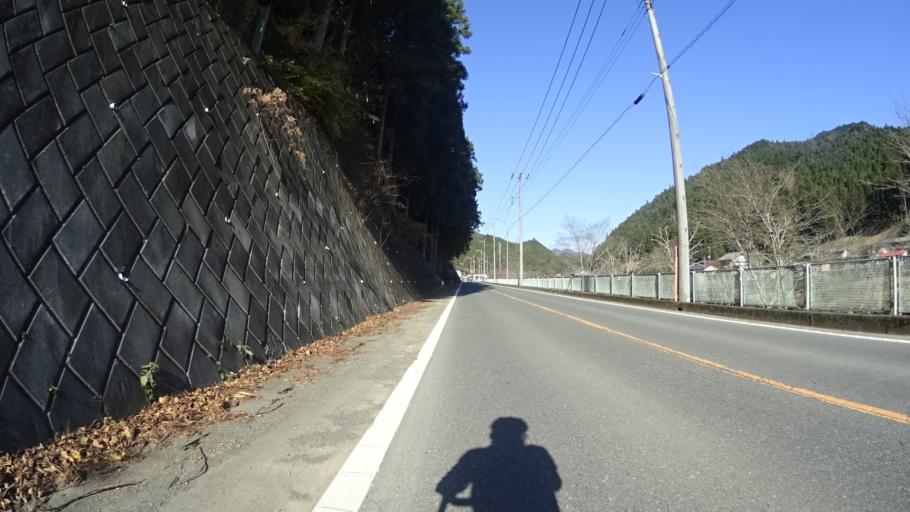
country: JP
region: Tokyo
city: Ome
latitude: 35.8586
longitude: 139.1894
